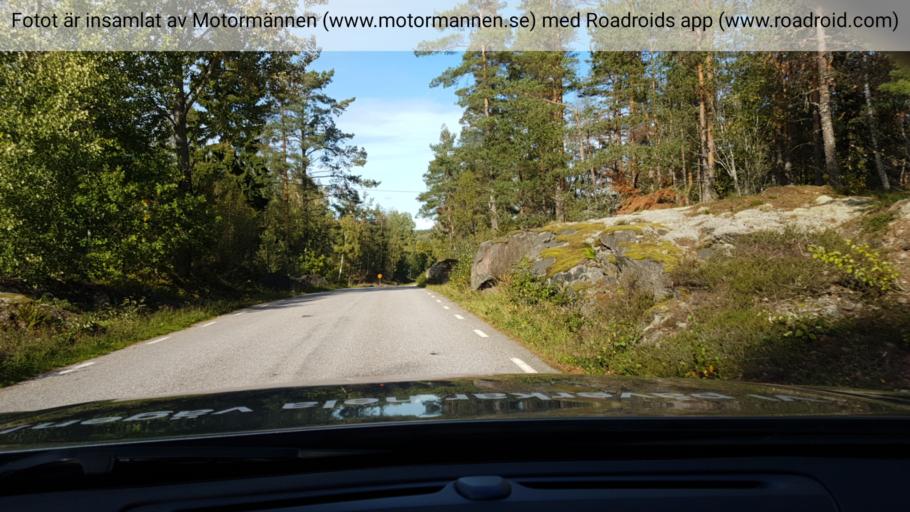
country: SE
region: OEstergoetland
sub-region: Valdemarsviks Kommun
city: Valdemarsvik
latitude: 58.0690
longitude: 16.6442
